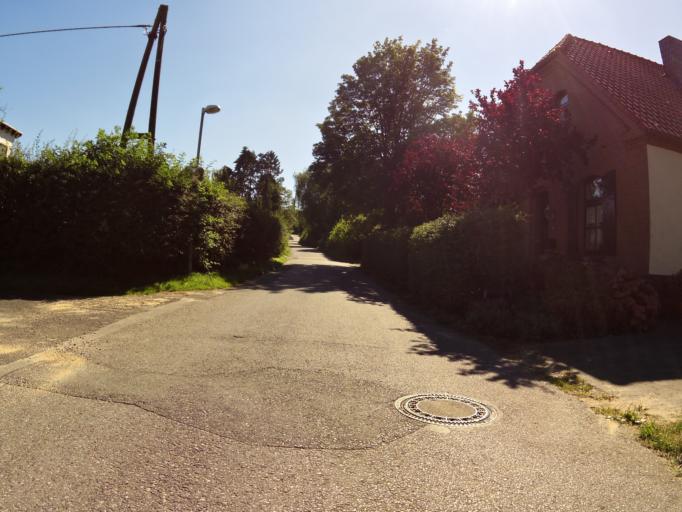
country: DE
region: North Rhine-Westphalia
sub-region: Regierungsbezirk Dusseldorf
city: Kranenburg
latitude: 51.7781
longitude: 6.0128
